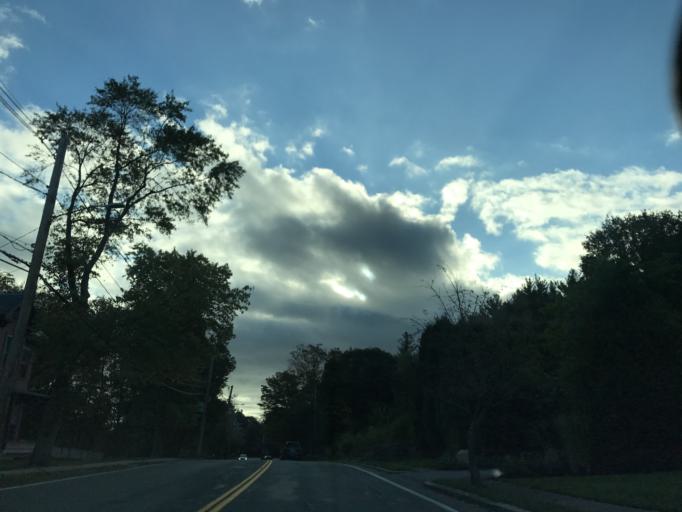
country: US
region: Massachusetts
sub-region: Suffolk County
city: Jamaica Plain
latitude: 42.3099
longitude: -71.1375
